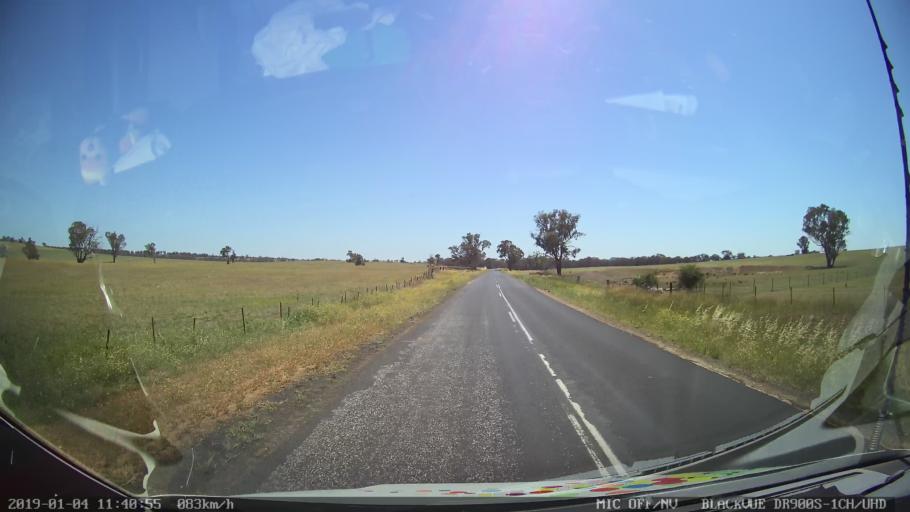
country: AU
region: New South Wales
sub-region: Cabonne
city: Molong
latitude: -32.9999
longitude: 148.7860
